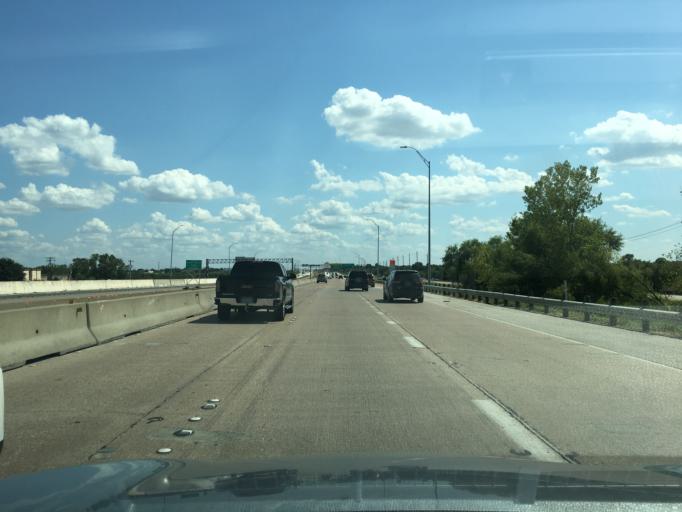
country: US
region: Texas
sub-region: Tarrant County
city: Arlington
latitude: 32.6699
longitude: -97.0629
